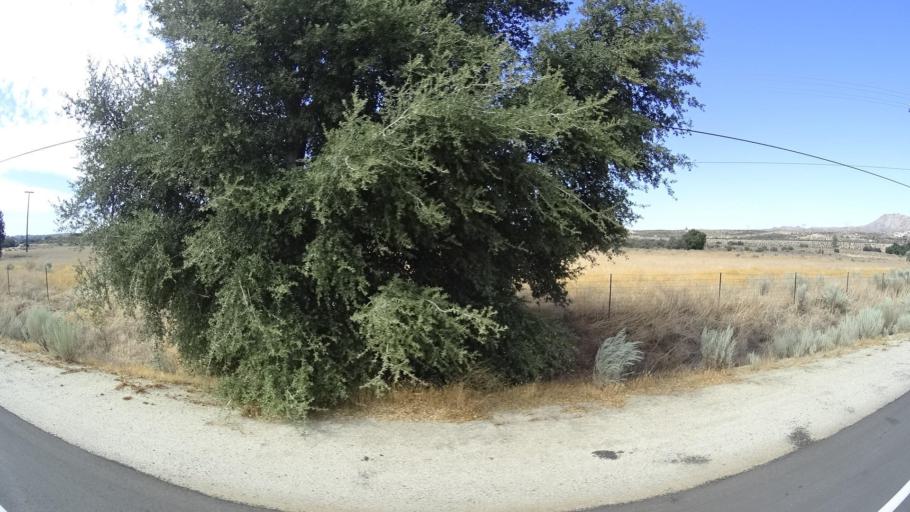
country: MX
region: Baja California
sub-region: Tecate
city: Cereso del Hongo
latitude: 32.6635
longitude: -116.2671
